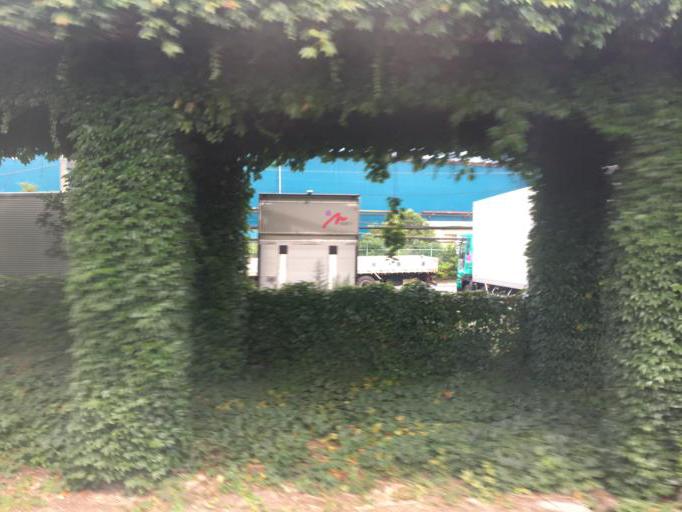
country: JP
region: Kanagawa
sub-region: Kawasaki-shi
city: Kawasaki
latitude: 35.5071
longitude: 139.7101
